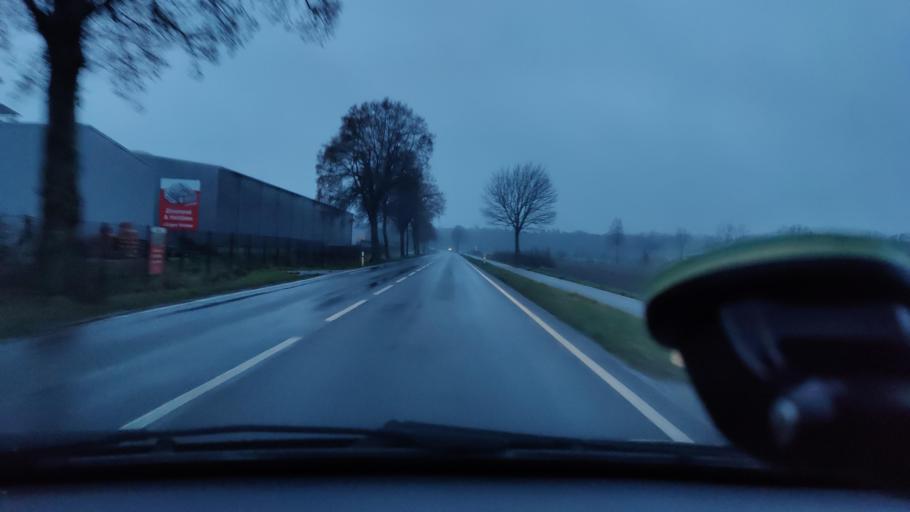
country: DE
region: North Rhine-Westphalia
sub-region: Regierungsbezirk Dusseldorf
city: Sonsbeck
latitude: 51.5994
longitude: 6.3813
